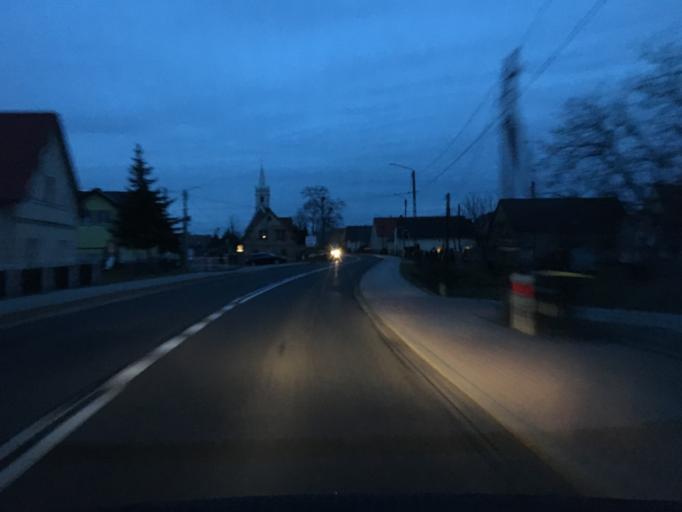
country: PL
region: Opole Voivodeship
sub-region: Powiat brzeski
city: Lewin Brzeski
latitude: 50.7742
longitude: 17.6290
